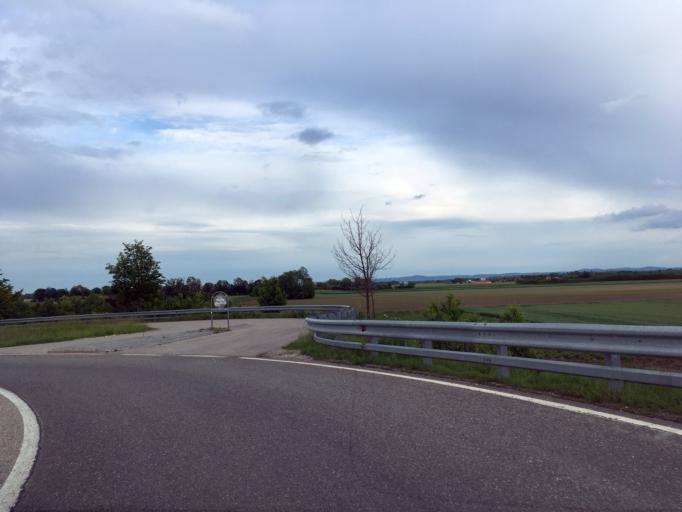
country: AT
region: Lower Austria
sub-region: Politischer Bezirk Tulln
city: Kirchberg am Wagram
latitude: 48.4049
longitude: 15.8802
